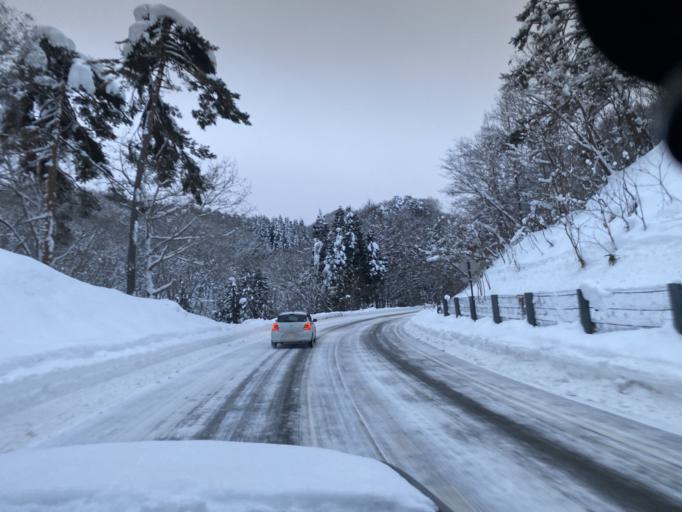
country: JP
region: Nagano
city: Omachi
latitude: 36.5835
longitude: 137.8845
